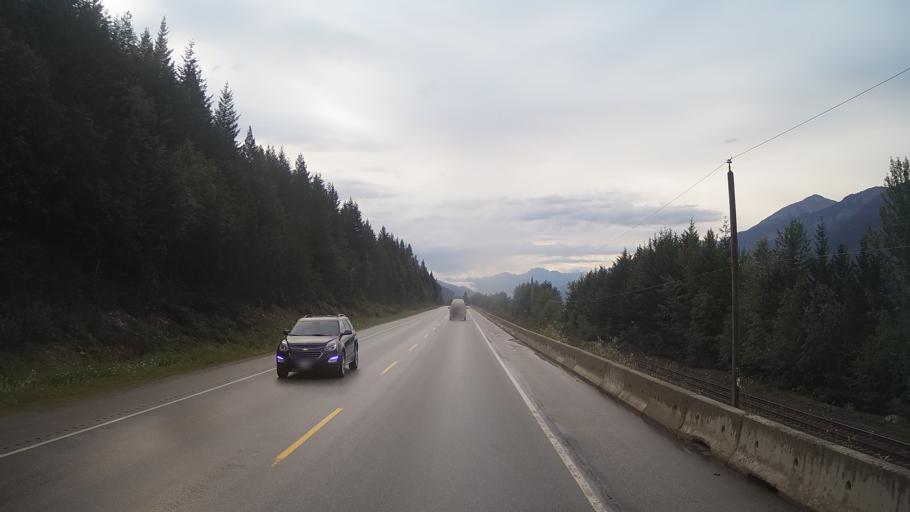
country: CA
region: Alberta
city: Jasper Park Lodge
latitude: 52.9597
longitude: -118.9037
